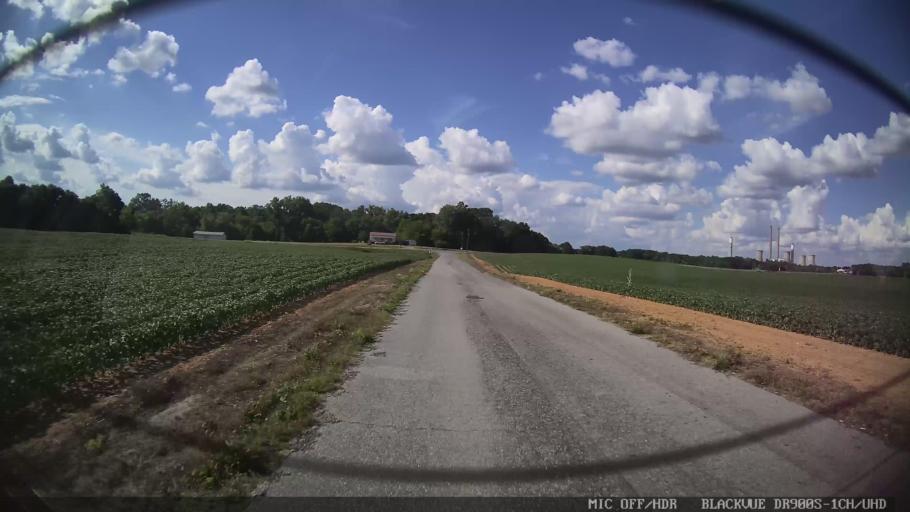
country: US
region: Georgia
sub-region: Bartow County
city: Euharlee
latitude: 34.1078
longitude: -84.9506
